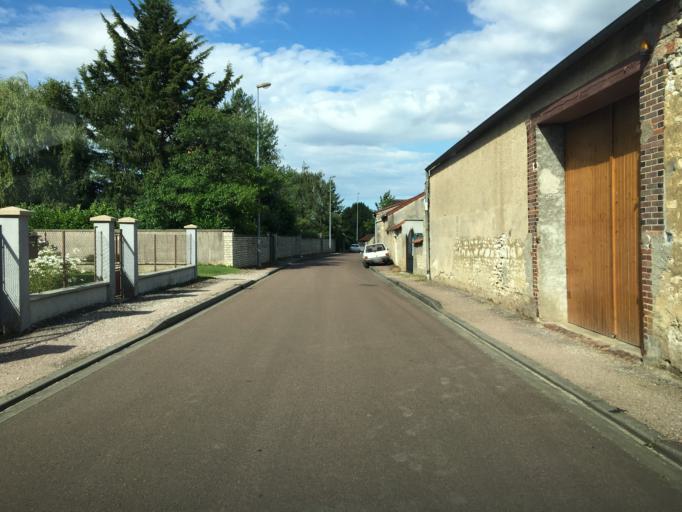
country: FR
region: Bourgogne
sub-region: Departement de l'Yonne
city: Appoigny
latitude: 47.8776
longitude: 3.5236
